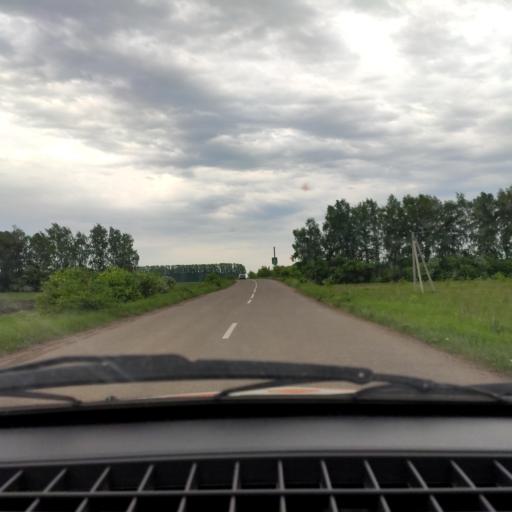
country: RU
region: Bashkortostan
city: Avdon
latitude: 54.5404
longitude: 55.7615
